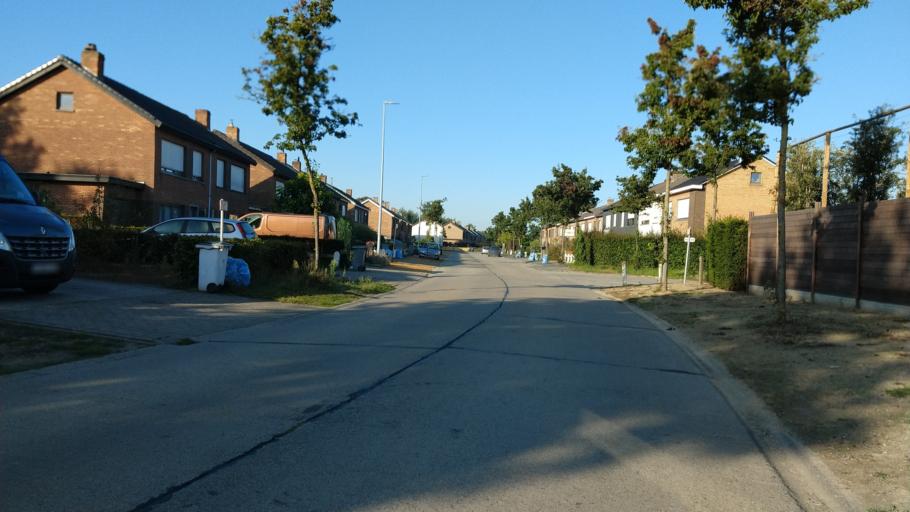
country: BE
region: Flanders
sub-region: Provincie Oost-Vlaanderen
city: Lochristi
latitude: 51.0868
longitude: 3.8576
